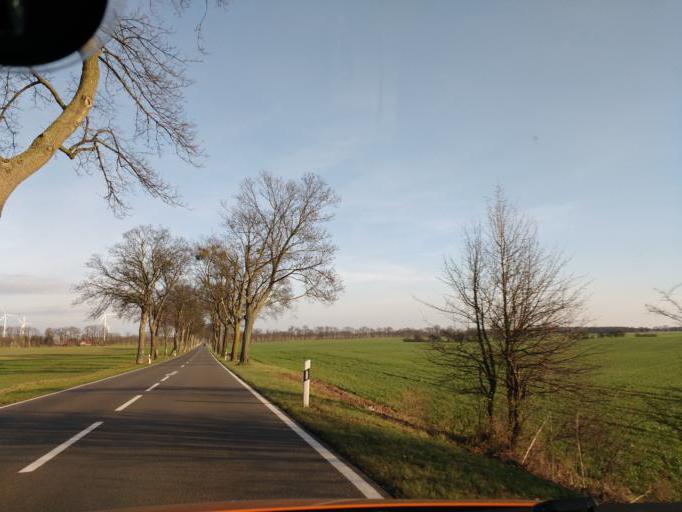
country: DE
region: Brandenburg
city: Protzel
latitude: 52.6633
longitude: 14.0489
